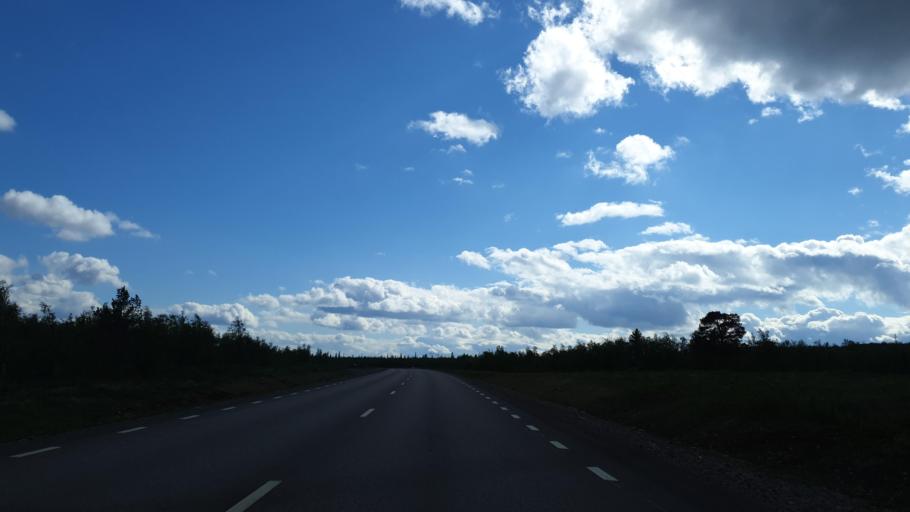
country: SE
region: Norrbotten
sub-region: Kiruna Kommun
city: Kiruna
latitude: 67.8134
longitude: 20.2393
